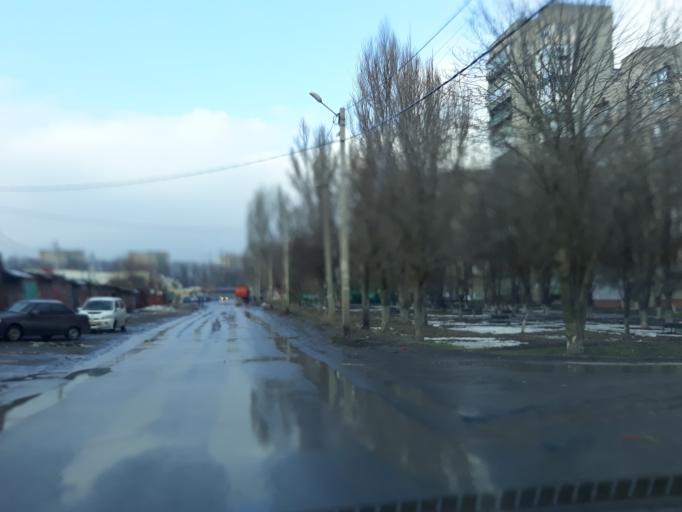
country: RU
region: Rostov
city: Taganrog
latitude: 47.2573
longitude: 38.9121
